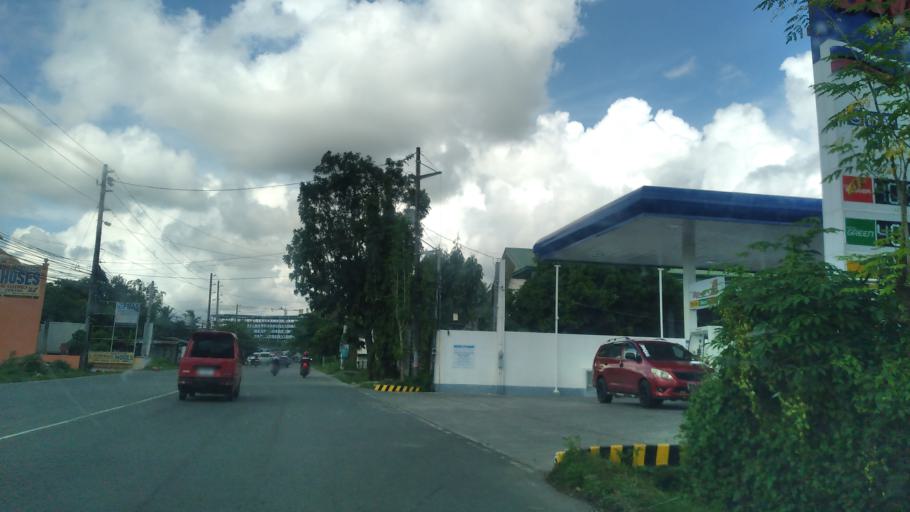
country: PH
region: Calabarzon
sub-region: Province of Quezon
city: Isabang
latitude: 13.9588
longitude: 121.5691
